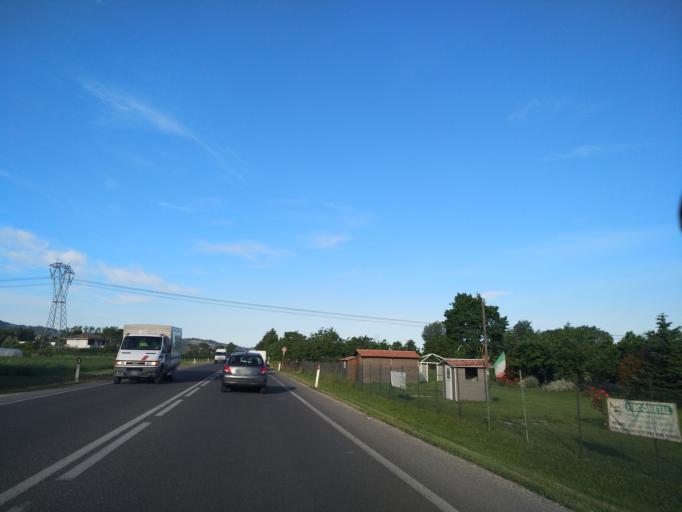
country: IT
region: The Marches
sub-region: Provincia di Pesaro e Urbino
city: Villa Ceccolini
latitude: 43.8788
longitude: 12.8499
